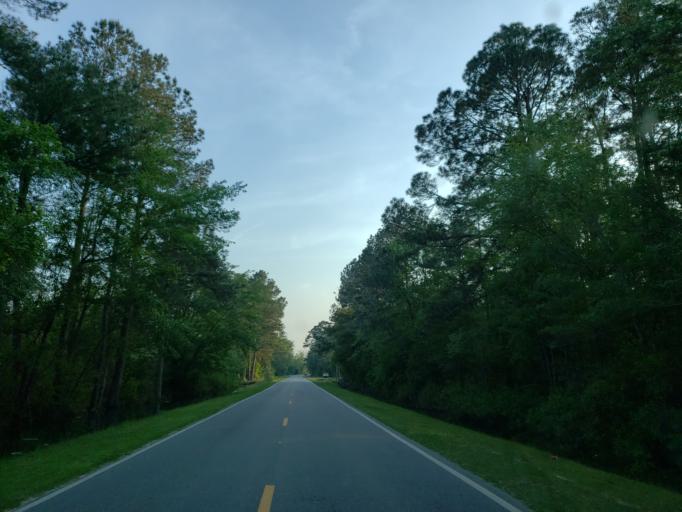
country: US
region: Georgia
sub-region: Cook County
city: Sparks
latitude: 31.1709
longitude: -83.4330
